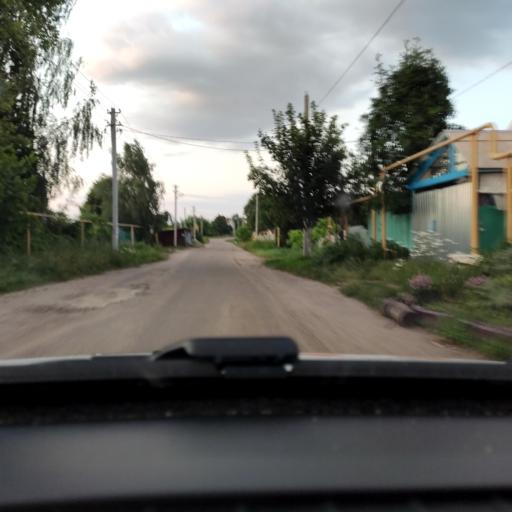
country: RU
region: Voronezj
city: Semiluki
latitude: 51.7449
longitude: 39.0183
